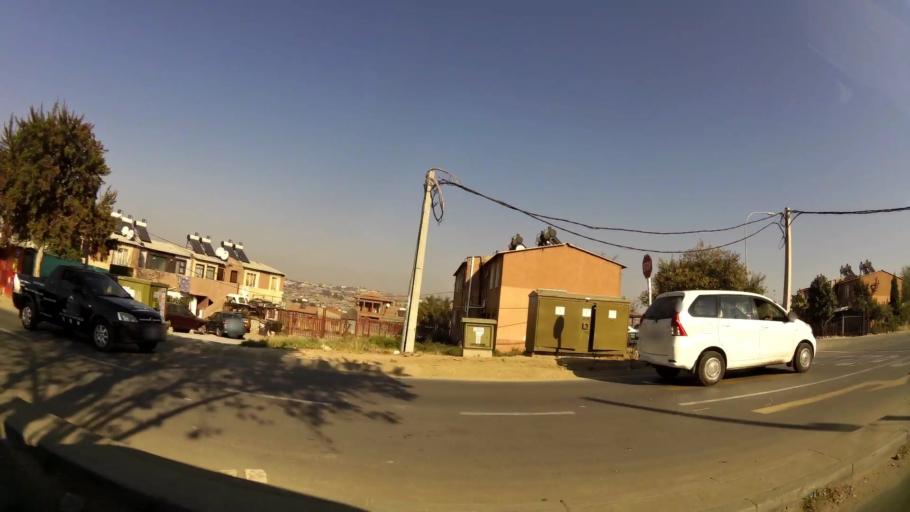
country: ZA
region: Gauteng
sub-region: City of Johannesburg Metropolitan Municipality
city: Modderfontein
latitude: -26.0992
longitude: 28.1169
